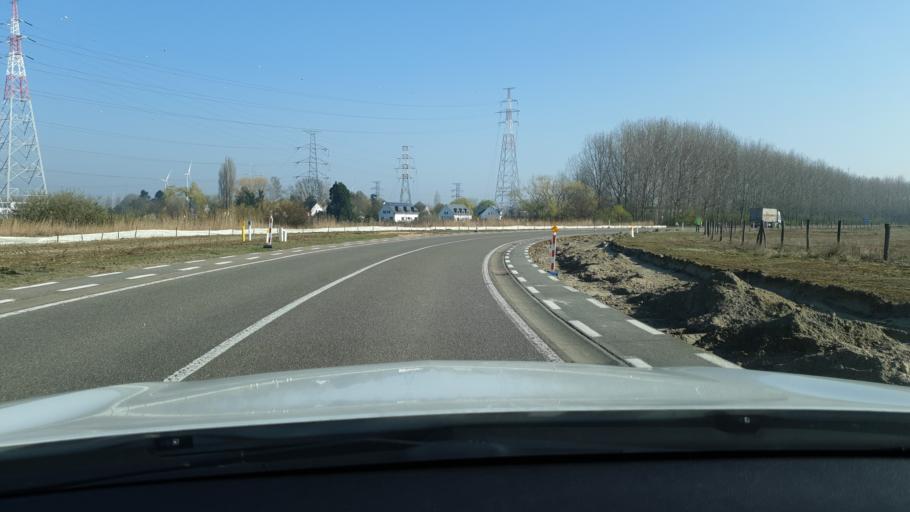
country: BE
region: Flanders
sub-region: Provincie Oost-Vlaanderen
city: Beveren
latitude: 51.2487
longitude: 4.2861
